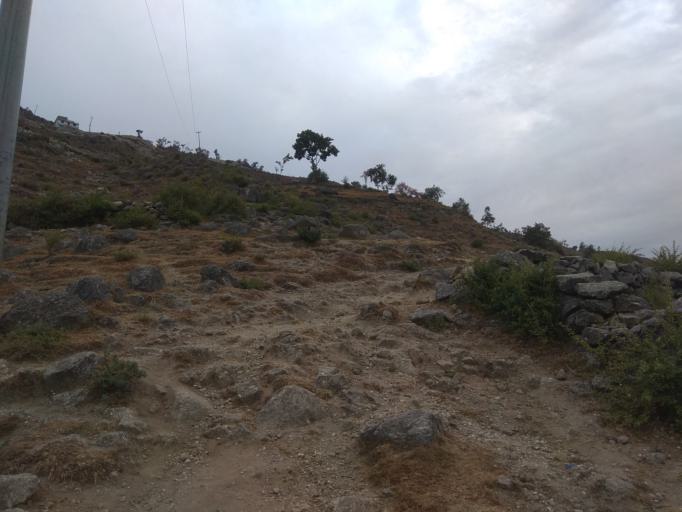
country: NP
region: Far Western
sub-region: Seti Zone
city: Achham
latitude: 29.2367
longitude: 81.6393
